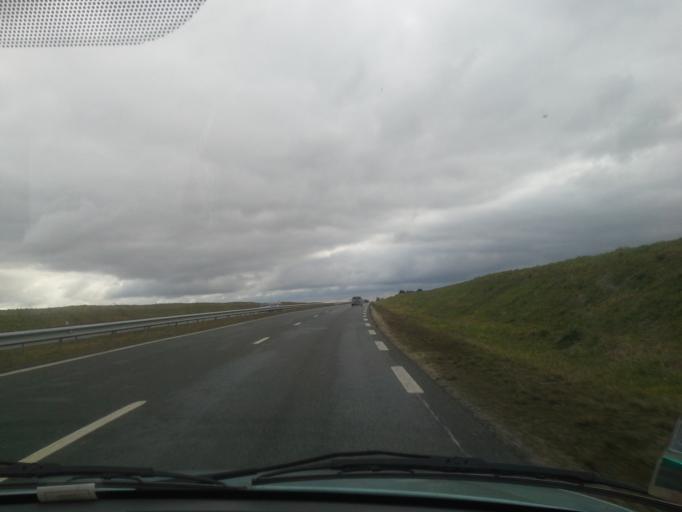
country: FR
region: Centre
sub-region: Departement du Loir-et-Cher
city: Vendome
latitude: 47.7316
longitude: 1.1491
